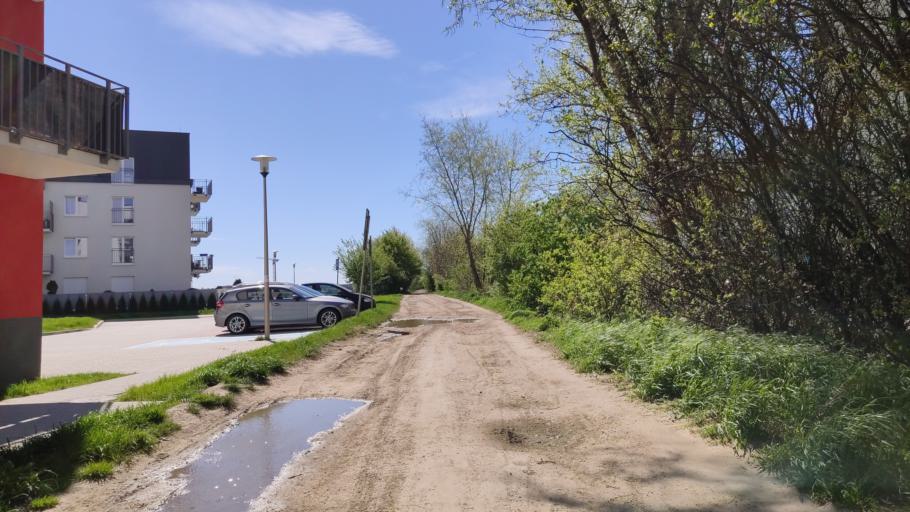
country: PL
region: Lower Silesian Voivodeship
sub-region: Powiat wroclawski
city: Zerniki Wroclawskie
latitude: 51.0612
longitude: 17.0435
